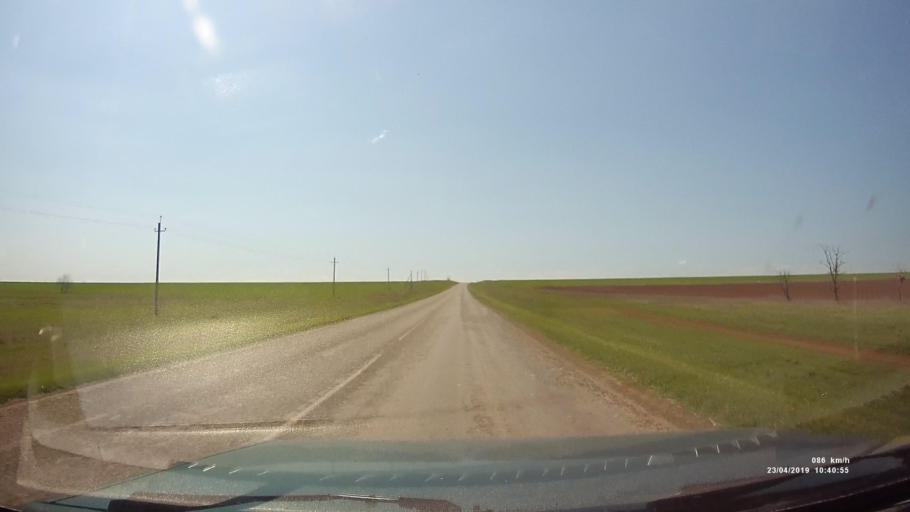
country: RU
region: Kalmykiya
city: Yashalta
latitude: 46.5003
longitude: 42.6384
